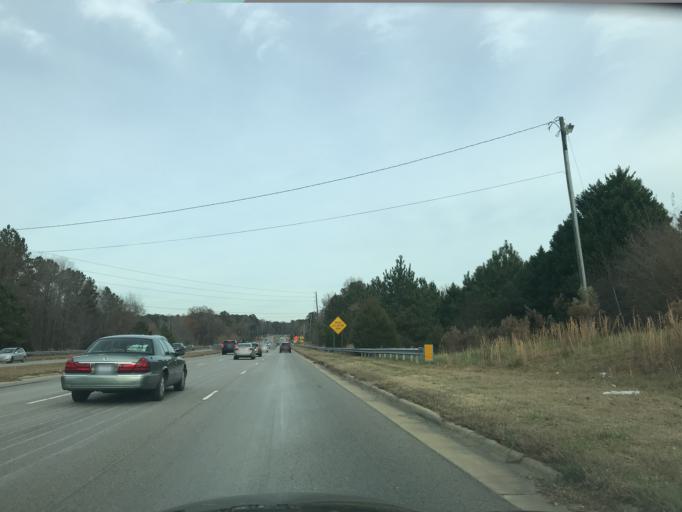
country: US
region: North Carolina
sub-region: Wake County
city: Rolesville
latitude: 35.8821
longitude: -78.5302
